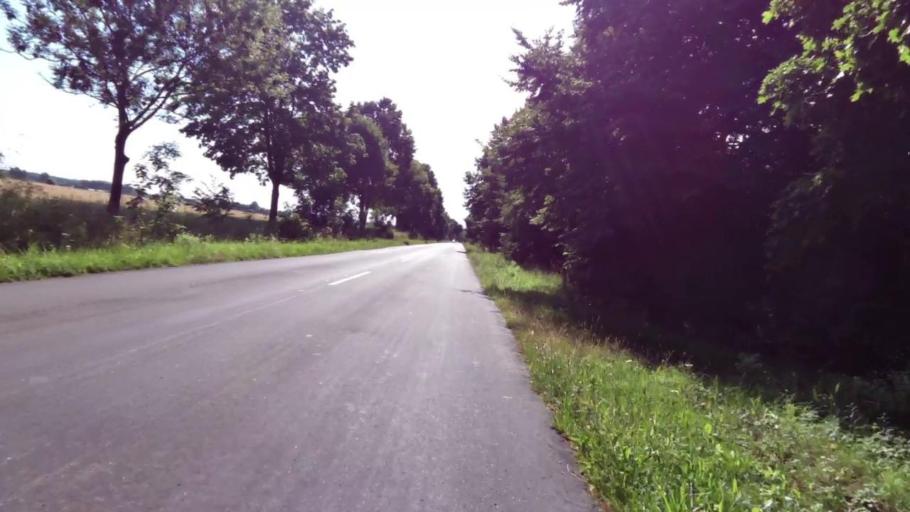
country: PL
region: West Pomeranian Voivodeship
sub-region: Powiat stargardzki
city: Dobrzany
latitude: 53.3652
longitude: 15.4079
